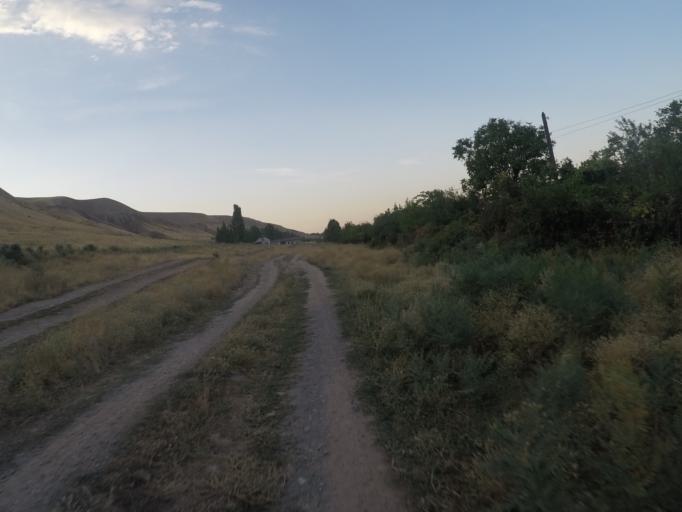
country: KG
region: Chuy
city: Bishkek
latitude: 42.7706
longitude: 74.6393
